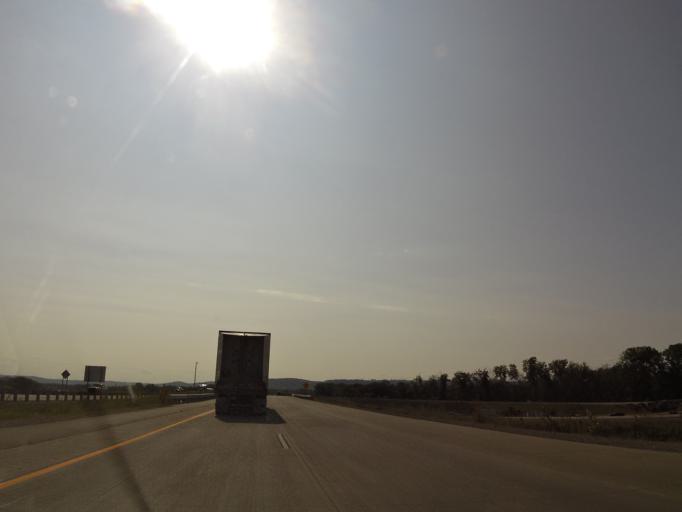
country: US
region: Wisconsin
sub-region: La Crosse County
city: Onalaska
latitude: 43.8652
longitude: -91.2338
